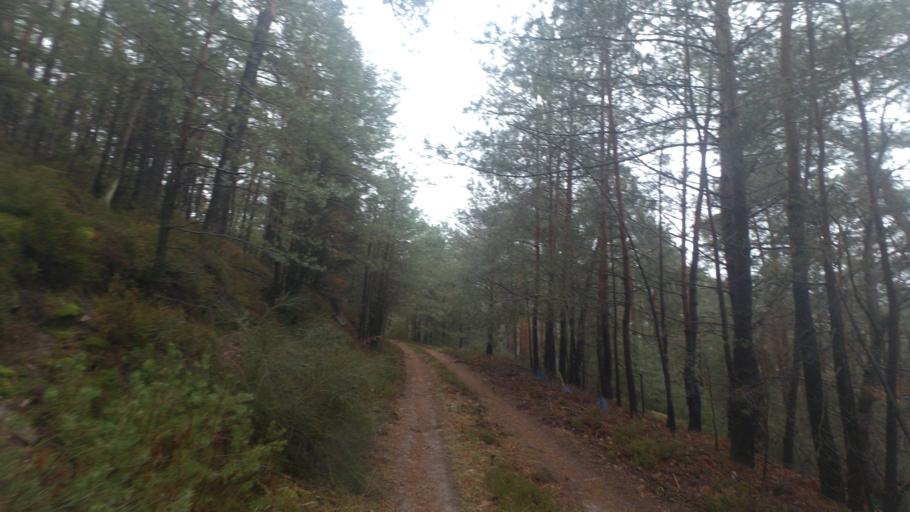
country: DE
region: Rheinland-Pfalz
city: Lindenberg
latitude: 49.3934
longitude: 8.1348
